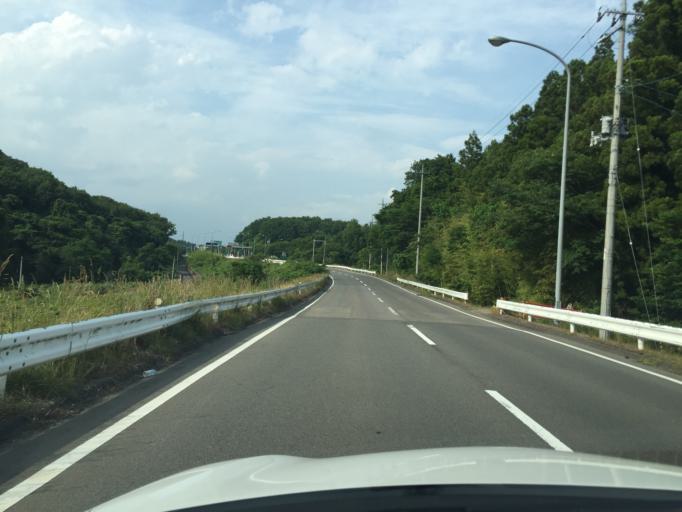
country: JP
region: Fukushima
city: Miharu
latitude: 37.4381
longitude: 140.4384
